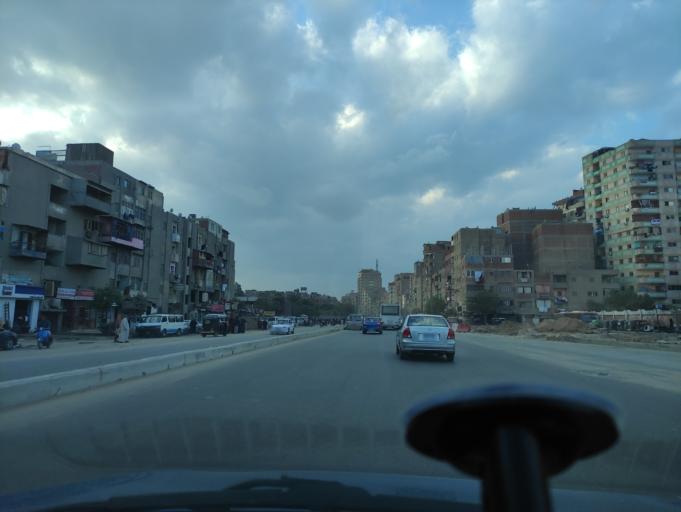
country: EG
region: Muhafazat al Qalyubiyah
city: Al Khankah
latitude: 30.1363
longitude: 31.3519
